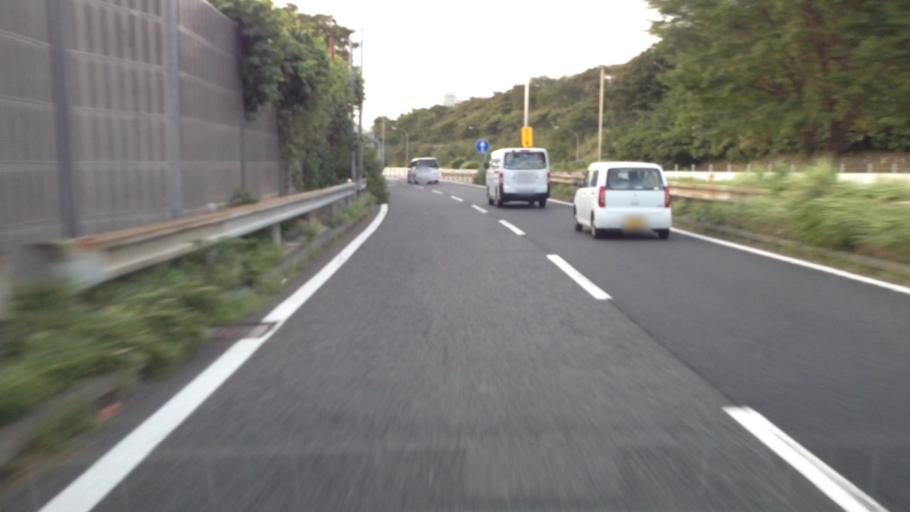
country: JP
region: Kanagawa
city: Yokohama
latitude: 35.4787
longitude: 139.5962
